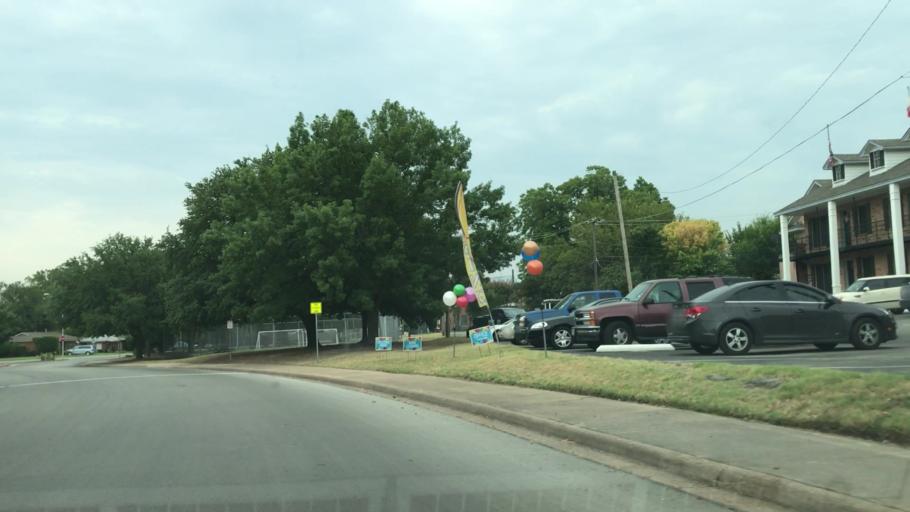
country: US
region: Texas
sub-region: Tarrant County
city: Hurst
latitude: 32.8249
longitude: -97.1682
